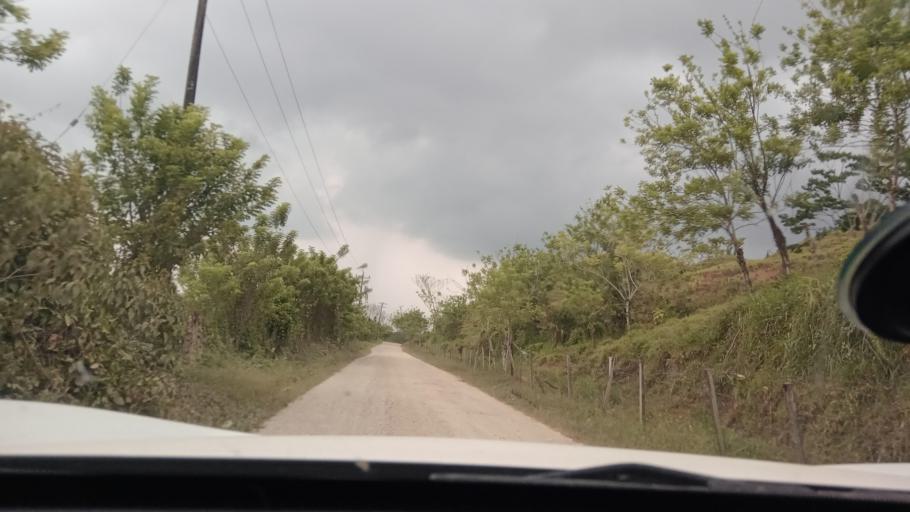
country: MX
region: Tabasco
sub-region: Huimanguillo
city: Francisco Rueda
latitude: 17.4377
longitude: -94.0581
